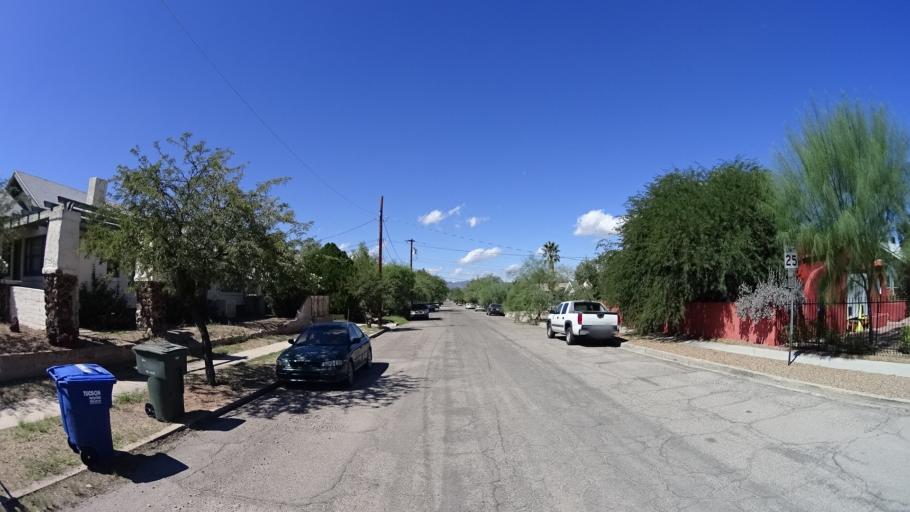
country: US
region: Arizona
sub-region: Pima County
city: Tucson
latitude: 32.2386
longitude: -110.9612
